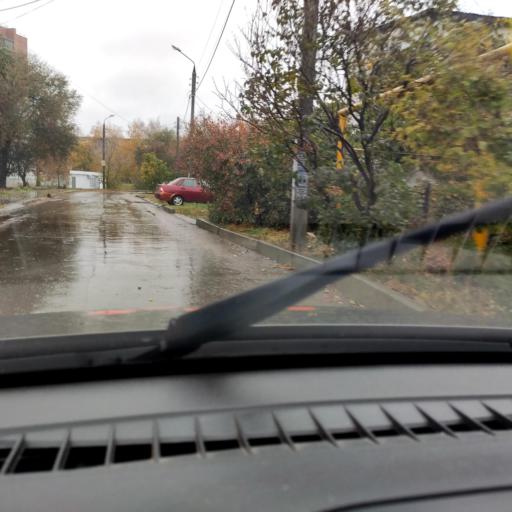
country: RU
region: Samara
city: Tol'yatti
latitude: 53.5285
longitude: 49.4036
